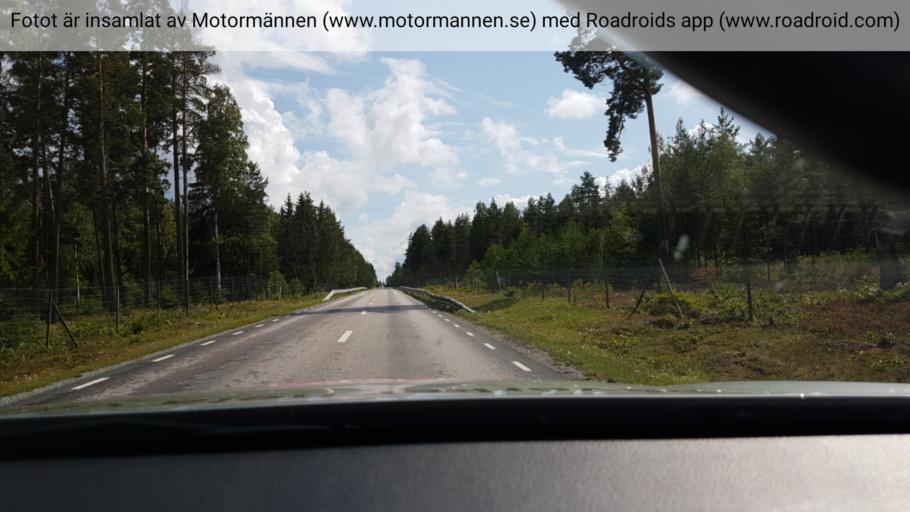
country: SE
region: Stockholm
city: Stenhamra
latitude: 59.3162
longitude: 17.6350
